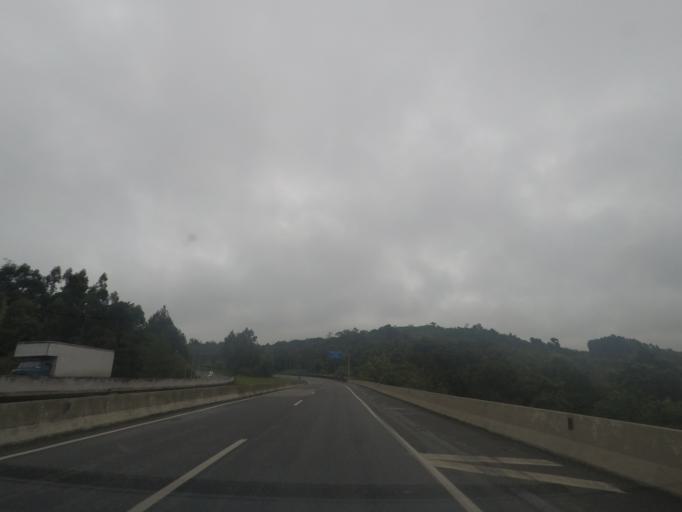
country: BR
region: Parana
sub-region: Antonina
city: Antonina
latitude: -25.0594
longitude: -48.5612
